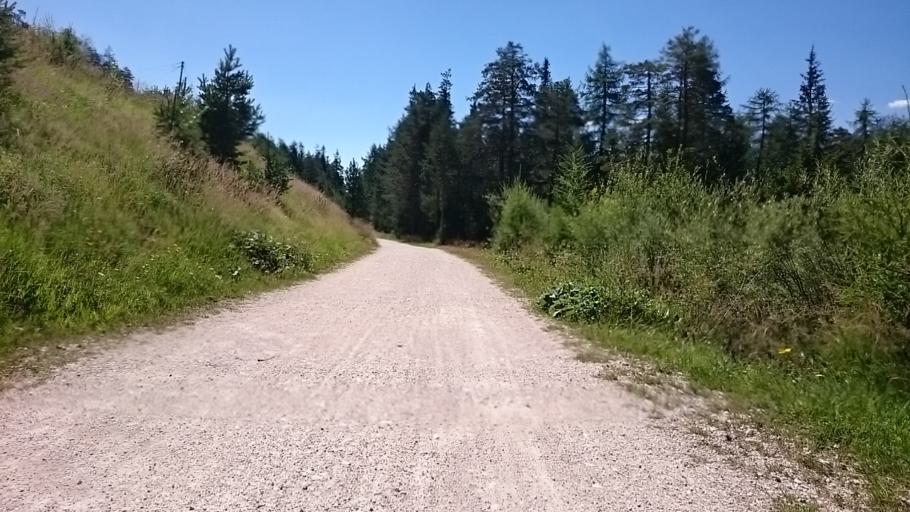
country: IT
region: Veneto
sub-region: Provincia di Belluno
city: Cortina d'Ampezzo
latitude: 46.5650
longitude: 12.1239
